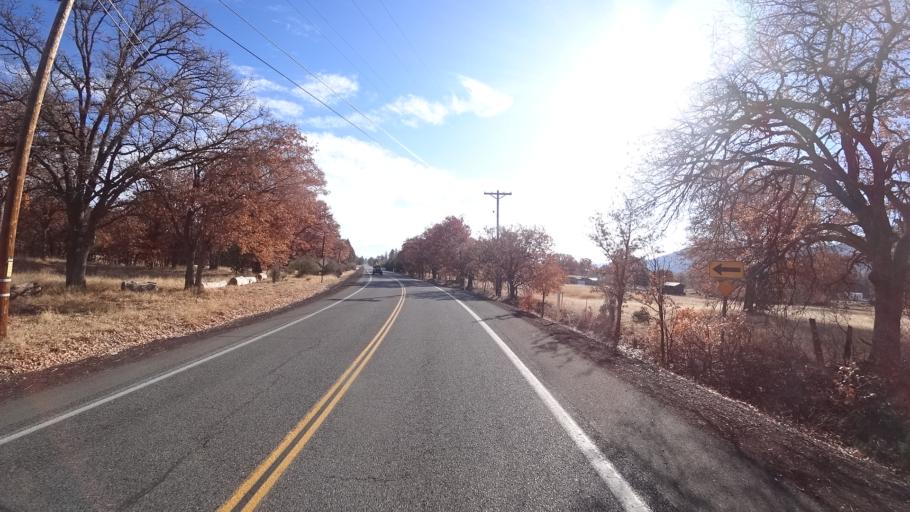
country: US
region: California
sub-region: Siskiyou County
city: Yreka
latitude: 41.6607
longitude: -122.5978
